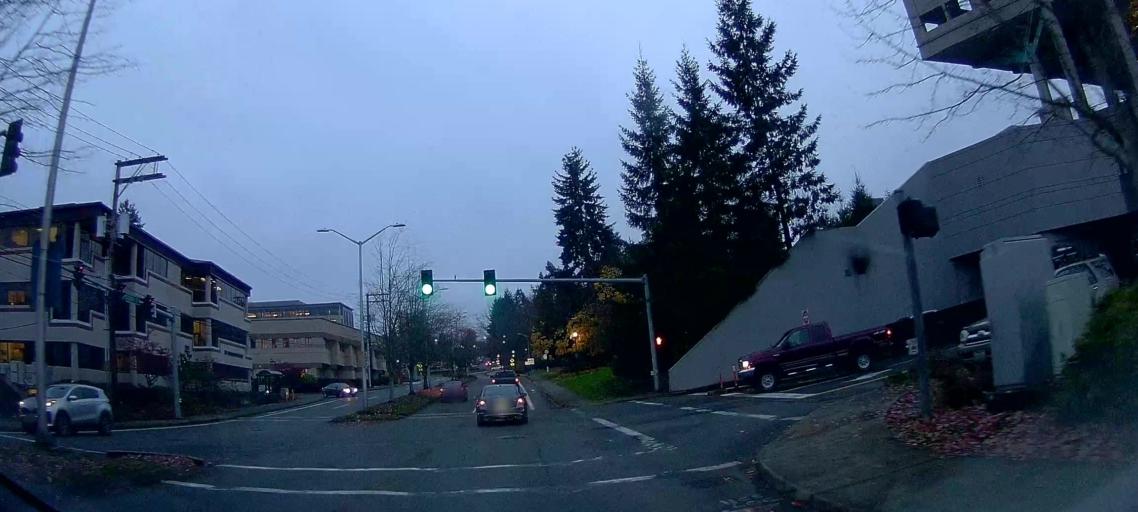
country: US
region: Washington
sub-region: Thurston County
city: Olympia
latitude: 47.0373
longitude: -122.8960
